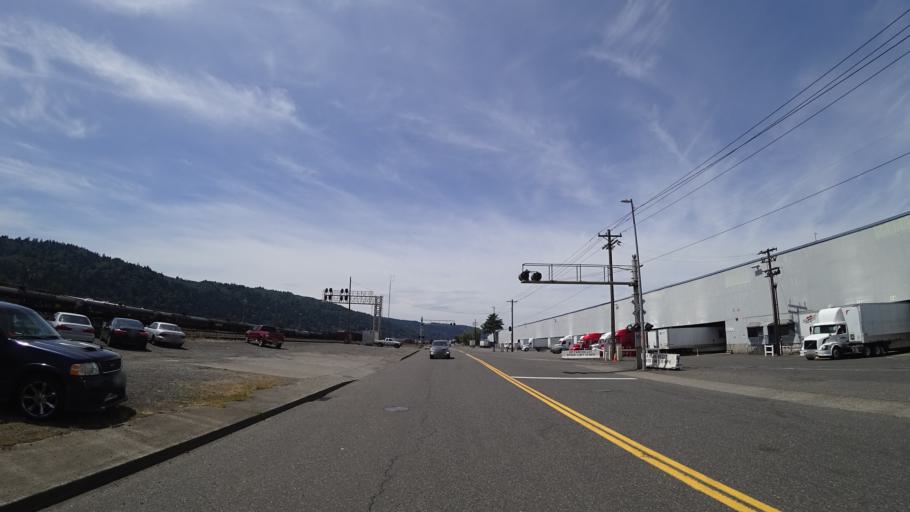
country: US
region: Oregon
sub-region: Multnomah County
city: Portland
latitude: 45.5498
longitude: -122.7091
